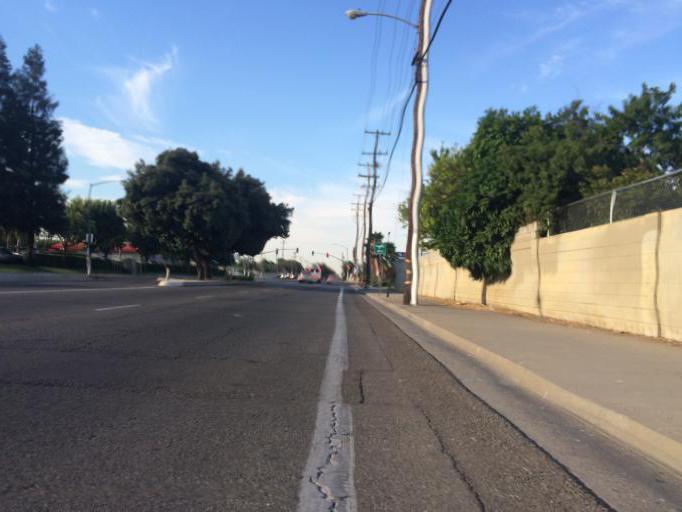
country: US
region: California
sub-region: Fresno County
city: Fresno
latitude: 36.7667
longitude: -119.7364
